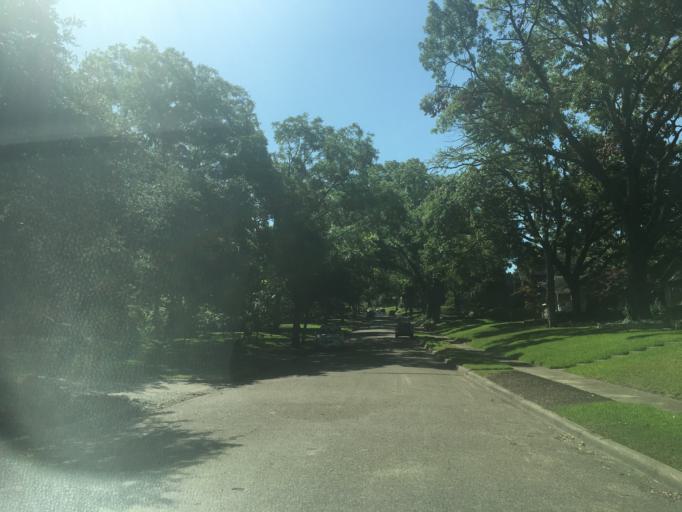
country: US
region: Texas
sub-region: Dallas County
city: Richardson
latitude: 32.8727
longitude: -96.7257
